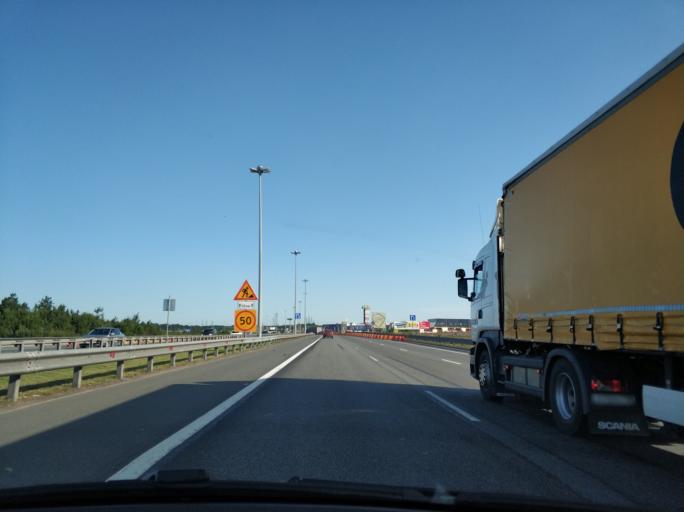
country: RU
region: Leningrad
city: Bugry
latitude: 60.0813
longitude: 30.3795
